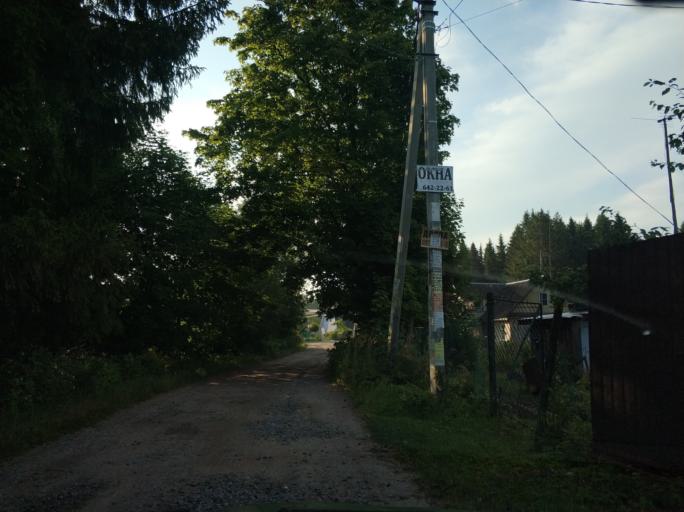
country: RU
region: Leningrad
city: Shcheglovo
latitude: 60.0525
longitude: 30.7474
